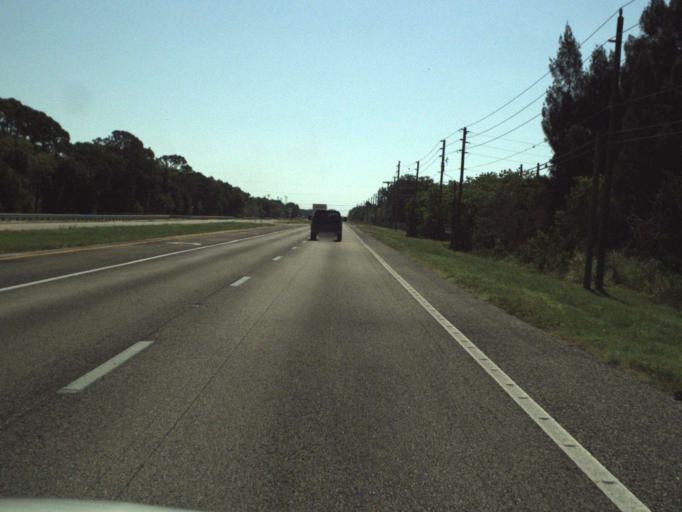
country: US
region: Florida
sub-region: Brevard County
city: Cocoa West
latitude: 28.3597
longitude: -80.8139
